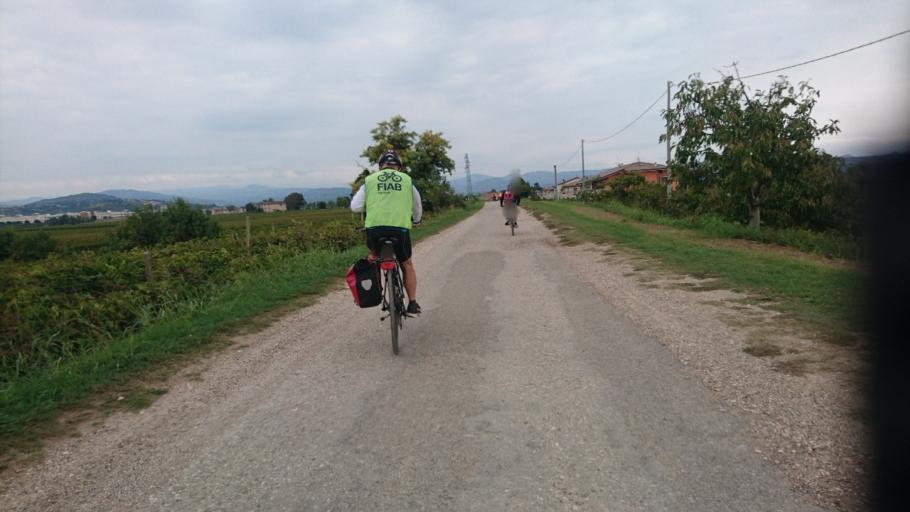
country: IT
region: Veneto
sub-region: Provincia di Verona
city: Caldierino-Rota
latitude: 45.4002
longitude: 11.1421
